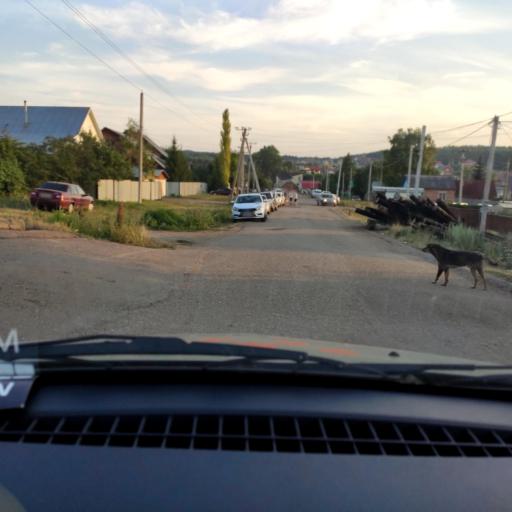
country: RU
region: Bashkortostan
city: Avdon
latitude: 54.5857
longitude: 55.6697
